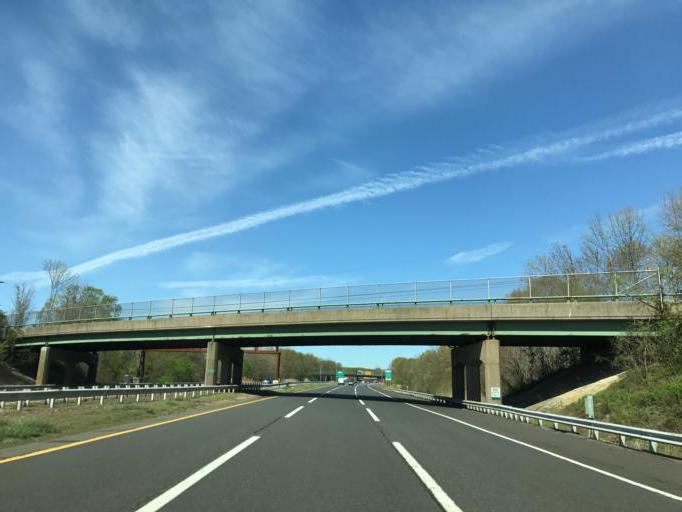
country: US
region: New Jersey
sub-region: Burlington County
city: Roebling
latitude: 40.0948
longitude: -74.7672
